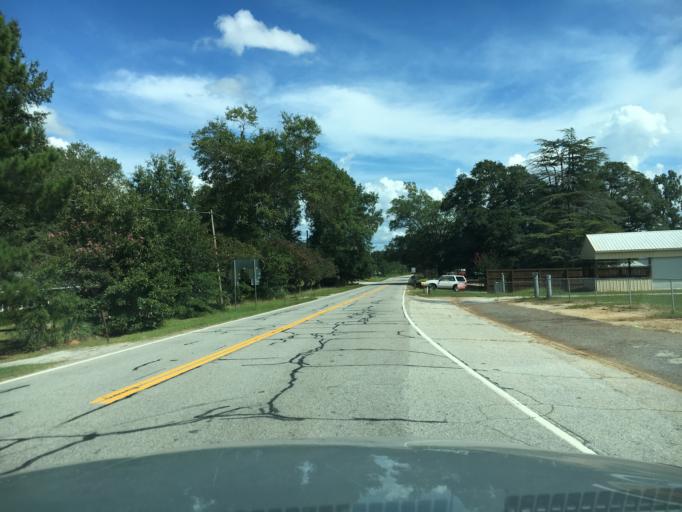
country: US
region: South Carolina
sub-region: Greenwood County
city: Ware Shoals
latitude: 34.4215
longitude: -82.2804
